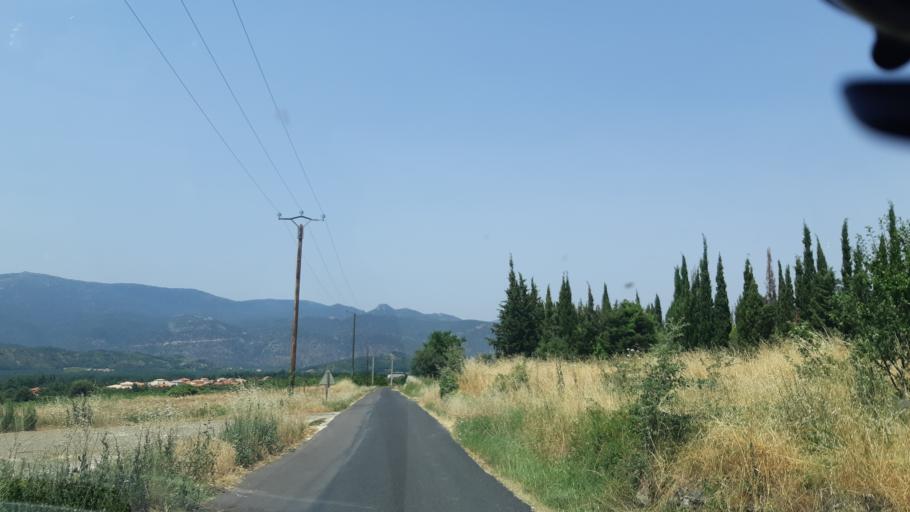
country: FR
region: Languedoc-Roussillon
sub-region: Departement des Pyrenees-Orientales
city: Vinca
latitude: 42.6134
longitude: 2.5177
